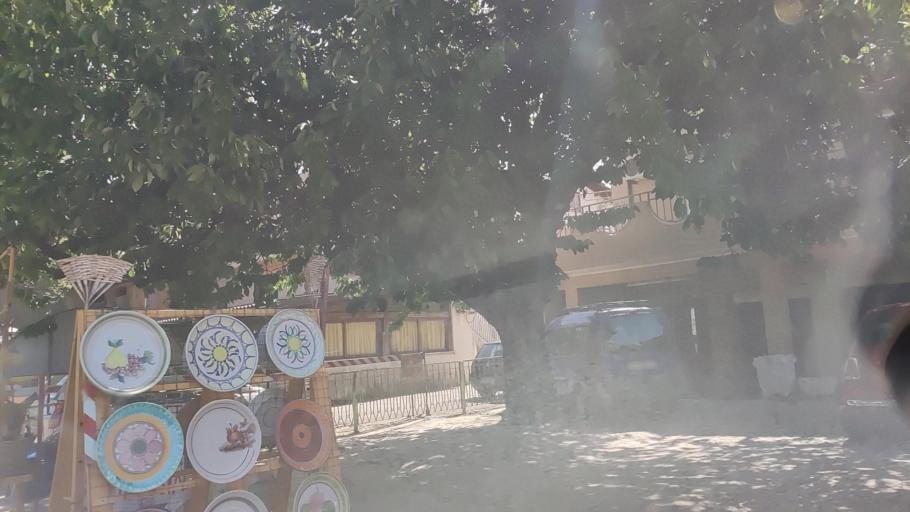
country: IT
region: Calabria
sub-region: Provincia di Reggio Calabria
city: Seminara
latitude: 38.3337
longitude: 15.8480
